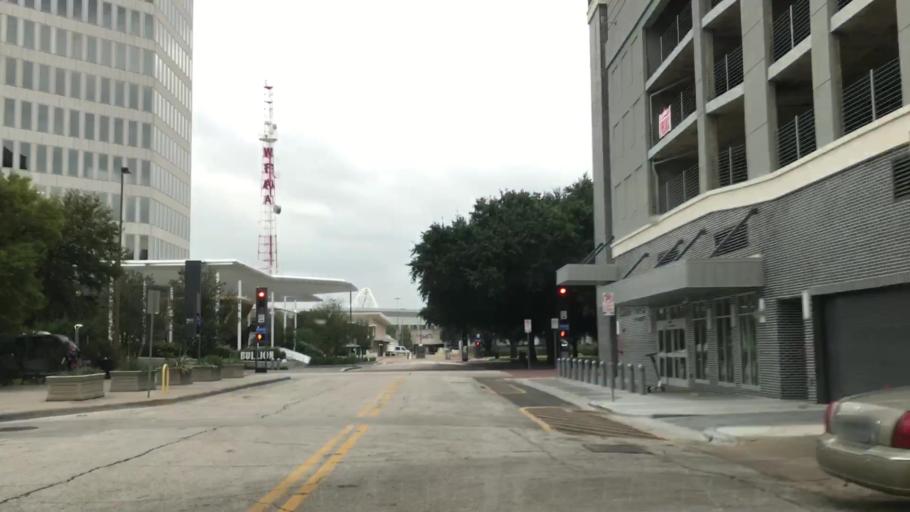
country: US
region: Texas
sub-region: Dallas County
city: Dallas
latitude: 32.7774
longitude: -96.8065
